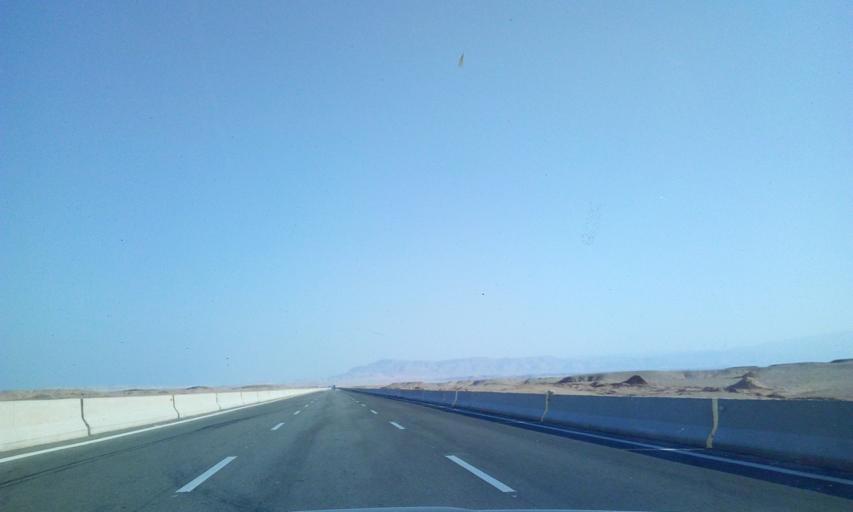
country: EG
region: As Suways
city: Ain Sukhna
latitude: 29.1549
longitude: 32.5137
